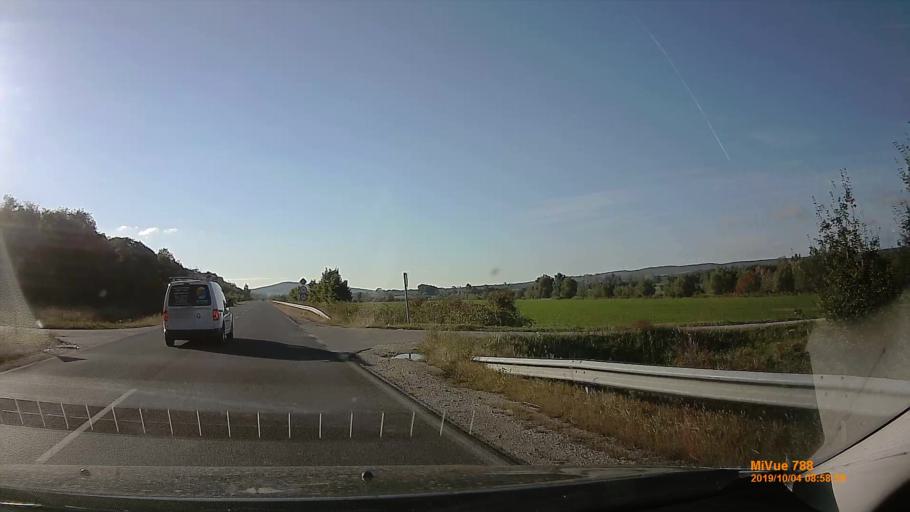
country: HU
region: Somogy
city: Balatonlelle
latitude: 46.7660
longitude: 17.7602
